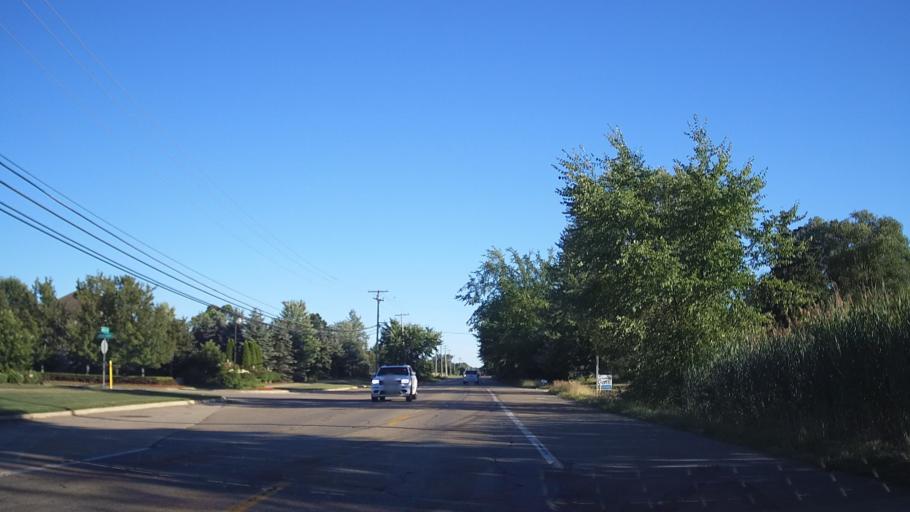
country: US
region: Michigan
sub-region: Macomb County
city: Shelby
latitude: 42.7133
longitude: -82.9596
